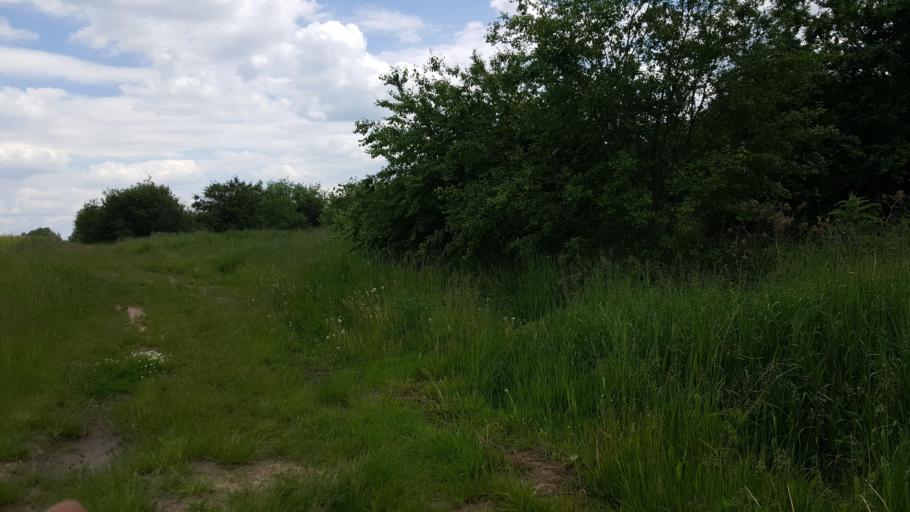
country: PL
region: Podlasie
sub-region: Powiat hajnowski
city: Bialowieza
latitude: 52.6655
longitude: 24.0869
